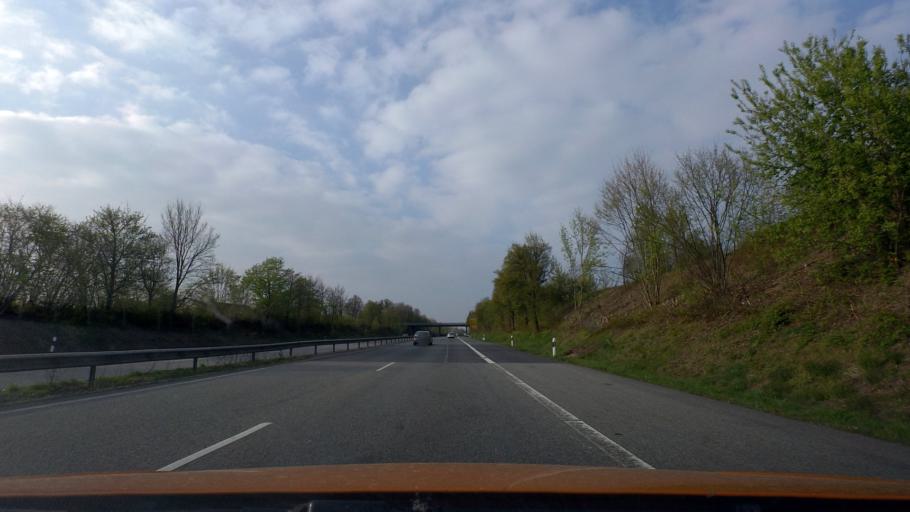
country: DE
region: North Rhine-Westphalia
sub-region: Regierungsbezirk Detmold
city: Herford
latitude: 52.1144
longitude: 8.6431
